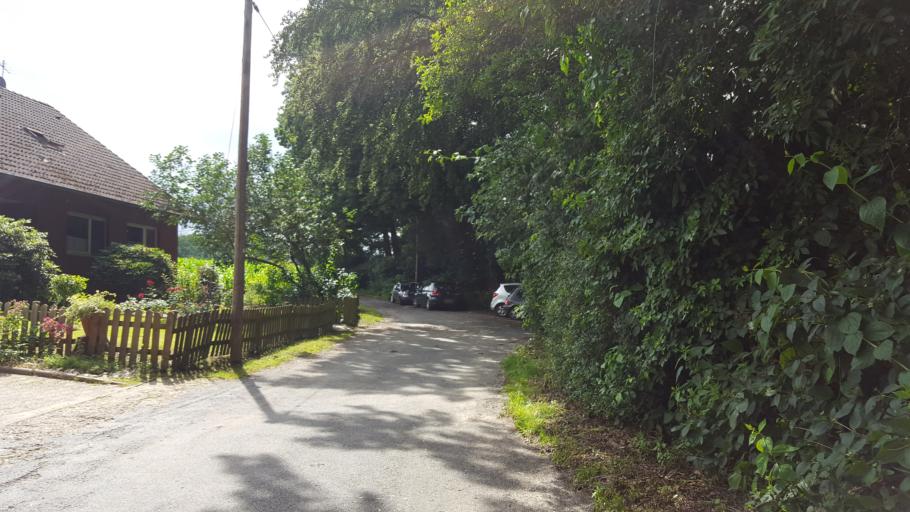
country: DE
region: North Rhine-Westphalia
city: Oer-Erkenschwick
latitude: 51.6446
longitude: 7.2869
